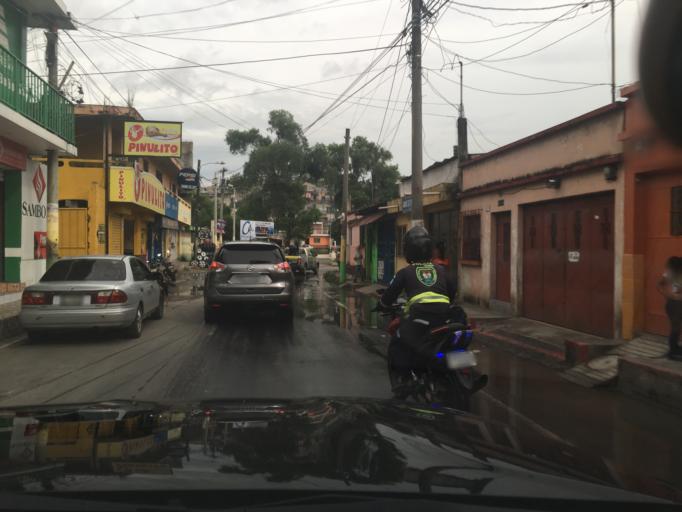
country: GT
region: Guatemala
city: Amatitlan
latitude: 14.4820
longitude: -90.6160
